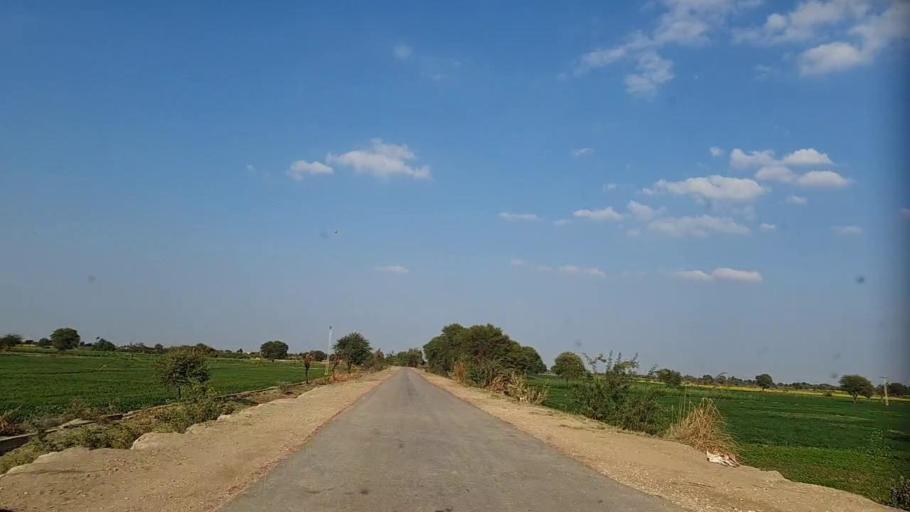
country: PK
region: Sindh
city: Pithoro
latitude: 25.6749
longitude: 69.2255
